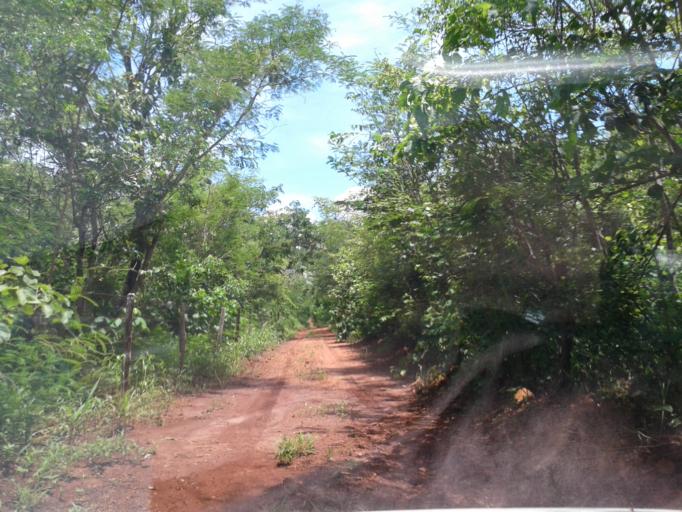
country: BR
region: Minas Gerais
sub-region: Santa Vitoria
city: Santa Vitoria
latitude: -19.1885
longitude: -50.6938
